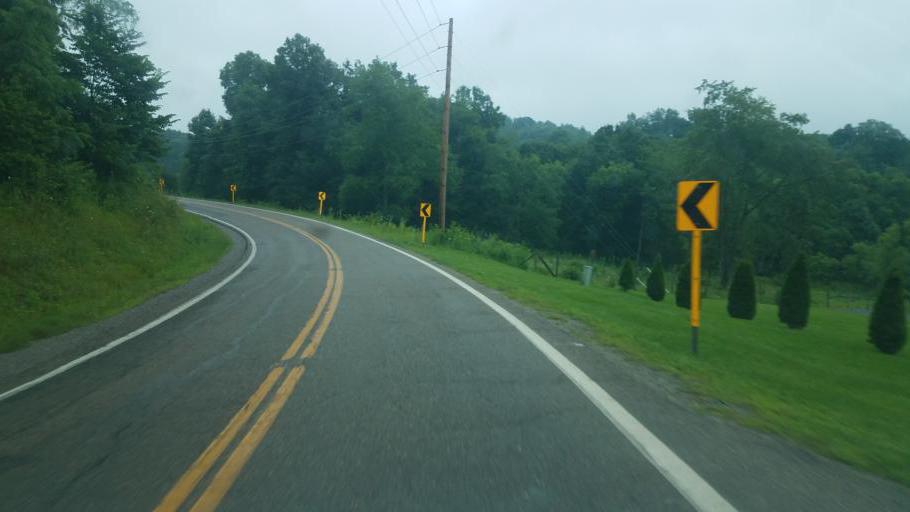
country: US
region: Ohio
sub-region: Carroll County
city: Carrollton
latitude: 40.4459
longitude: -81.0539
